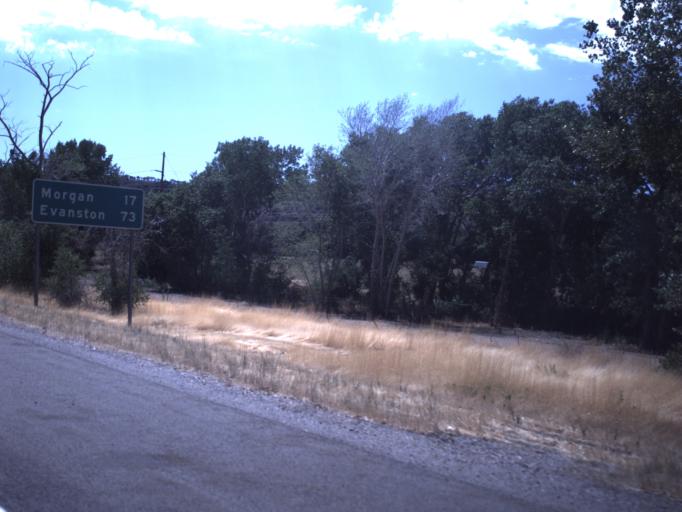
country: US
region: Utah
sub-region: Davis County
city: South Weber
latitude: 41.1397
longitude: -111.9545
